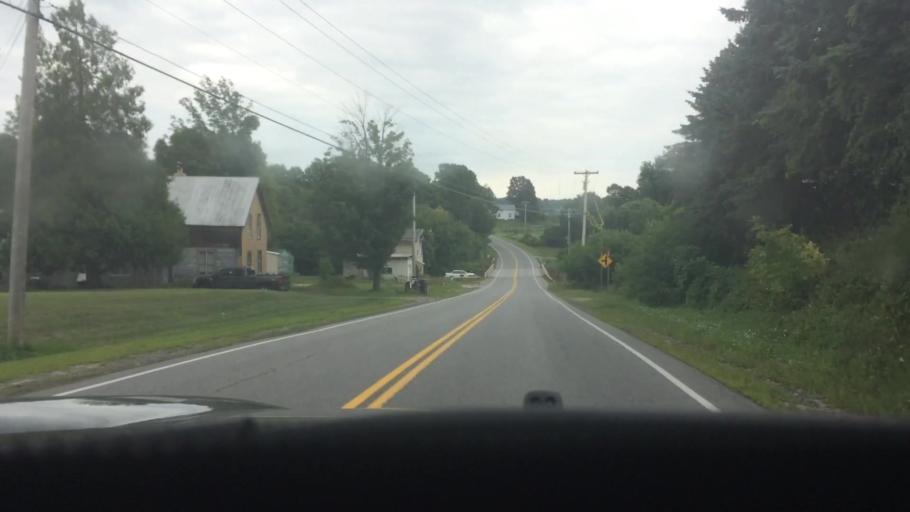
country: US
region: New York
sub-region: St. Lawrence County
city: Canton
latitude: 44.5574
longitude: -75.1145
